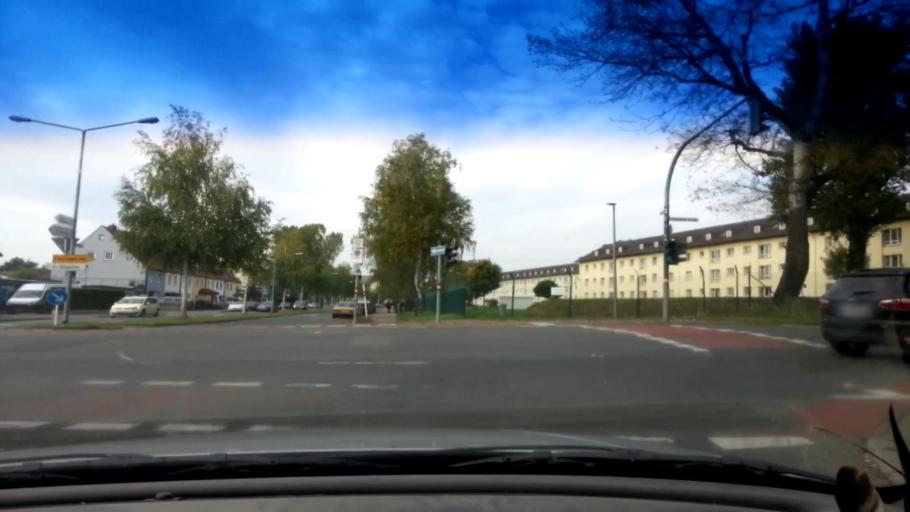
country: DE
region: Bavaria
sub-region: Upper Franconia
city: Bamberg
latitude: 49.9022
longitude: 10.9315
